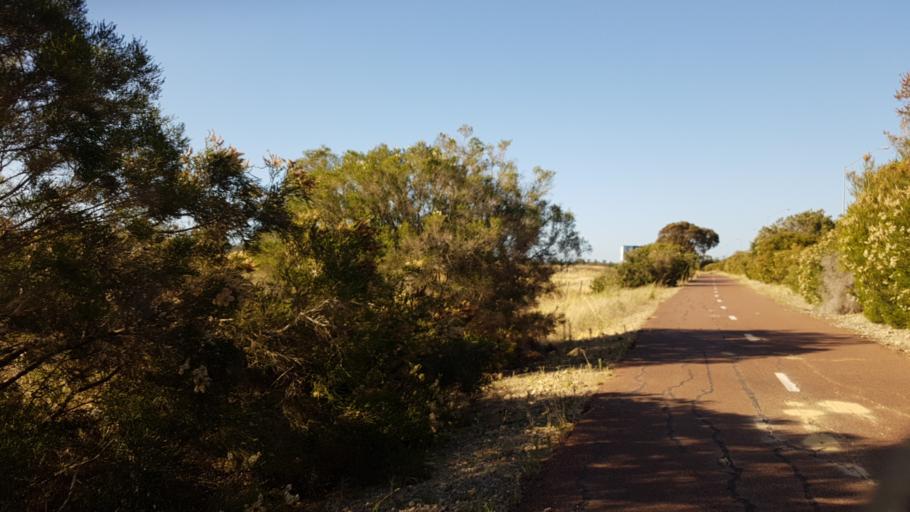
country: AU
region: Western Australia
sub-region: Kwinana
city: Wellard
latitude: -32.2830
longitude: 115.8382
